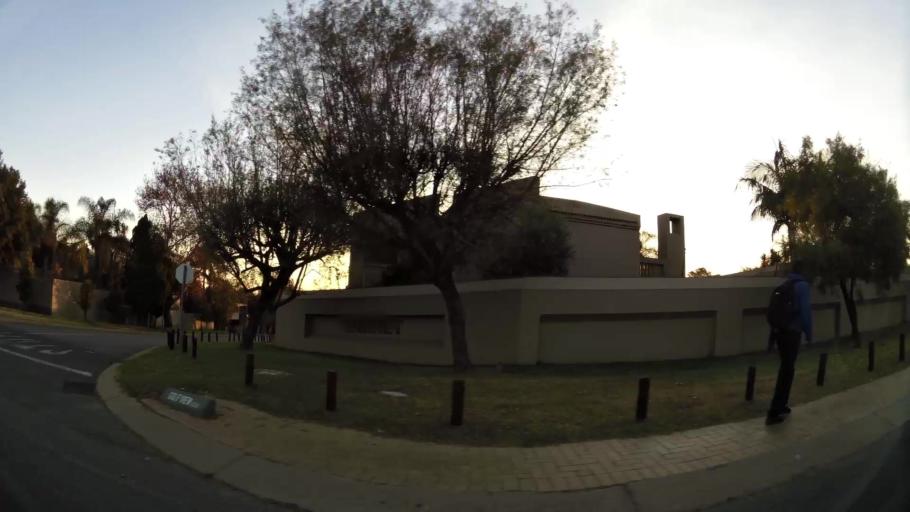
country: ZA
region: Gauteng
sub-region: City of Johannesburg Metropolitan Municipality
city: Midrand
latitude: -26.0540
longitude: 28.0861
